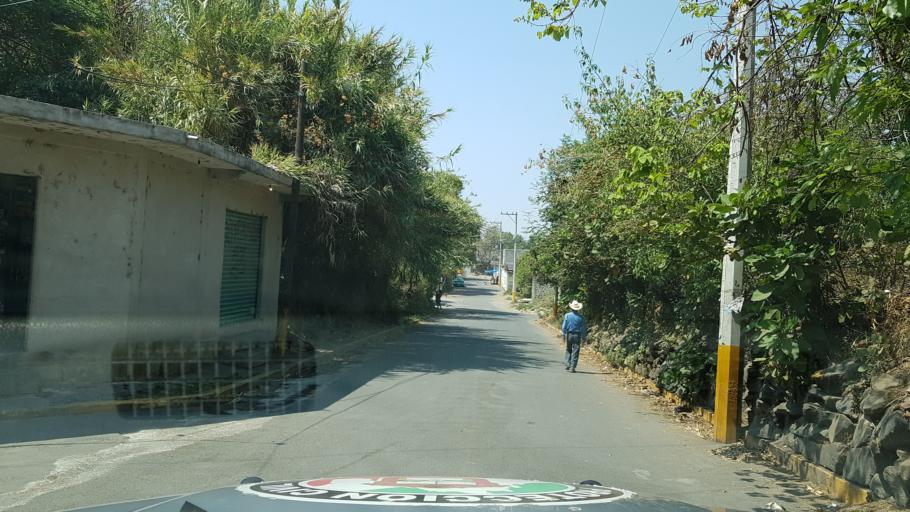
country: MX
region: Mexico
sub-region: Atlautla
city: San Andres Tlalamac
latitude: 18.9660
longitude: -98.8088
